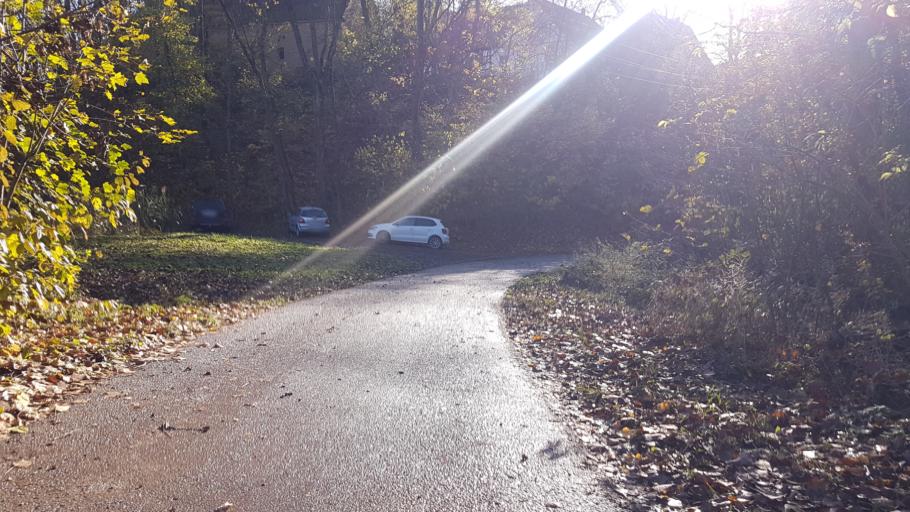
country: DE
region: Baden-Wuerttemberg
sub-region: Regierungsbezirk Stuttgart
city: Gemmingen
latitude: 49.1582
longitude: 8.9579
